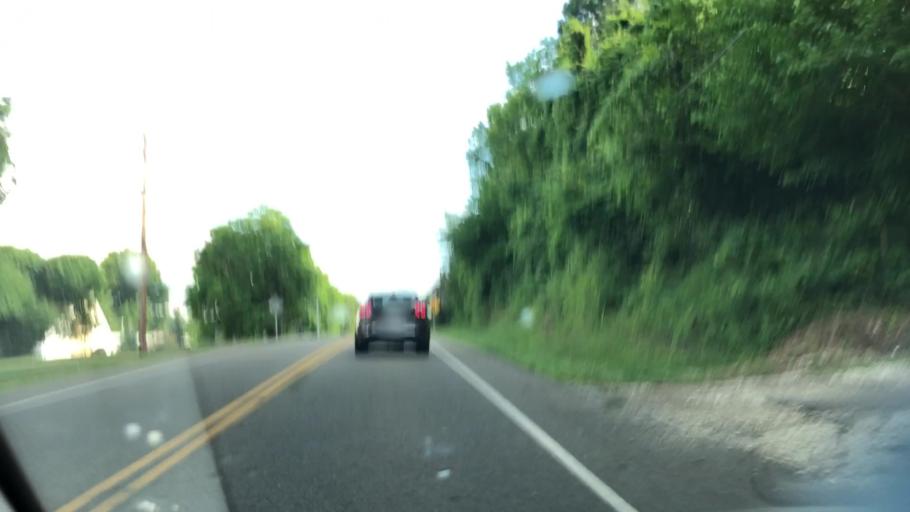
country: US
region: Ohio
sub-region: Summit County
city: Portage Lakes
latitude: 40.9835
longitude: -81.5462
